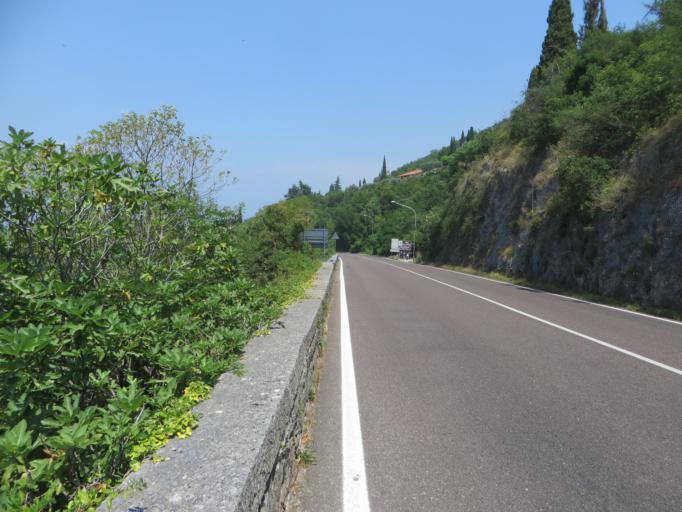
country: IT
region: Veneto
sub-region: Provincia di Verona
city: Torri del Benaco
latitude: 45.5813
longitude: 10.6739
